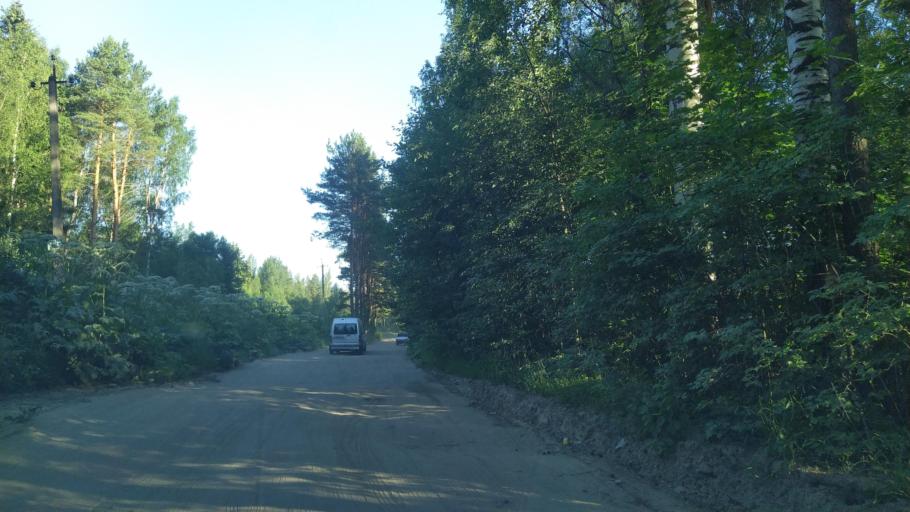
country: RU
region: Leningrad
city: Koltushi
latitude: 59.9110
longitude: 30.7359
